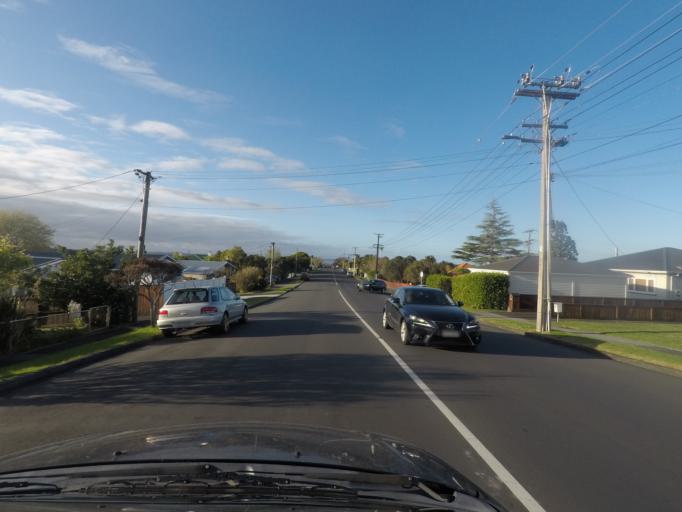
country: NZ
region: Auckland
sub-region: Auckland
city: Waitakere
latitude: -36.9159
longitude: 174.6579
